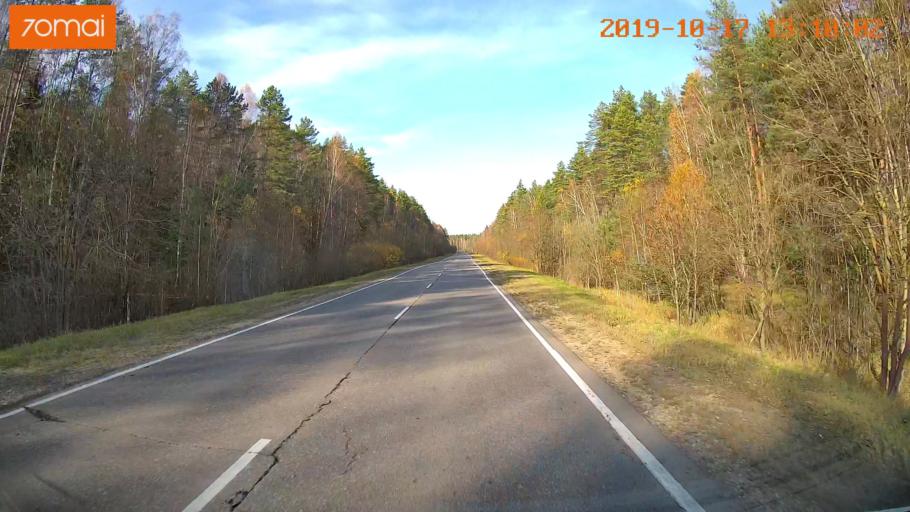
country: RU
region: Rjazan
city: Syntul
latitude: 55.0129
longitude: 41.2591
